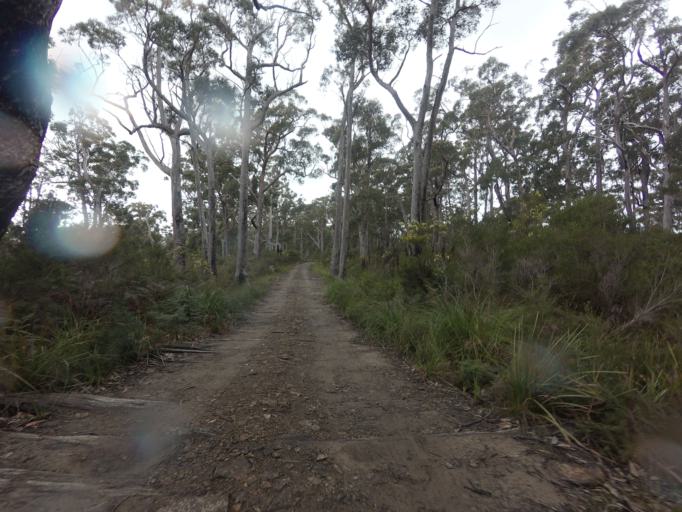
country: AU
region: Tasmania
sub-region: Huon Valley
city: Geeveston
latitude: -43.4651
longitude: 146.9222
